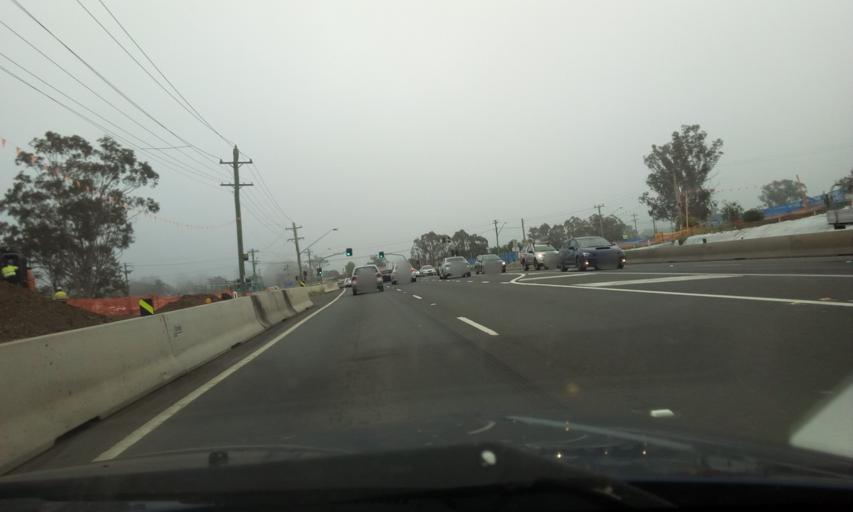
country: AU
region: New South Wales
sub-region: Penrith Municipality
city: Kingswood Park
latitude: -33.7769
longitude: 150.7117
